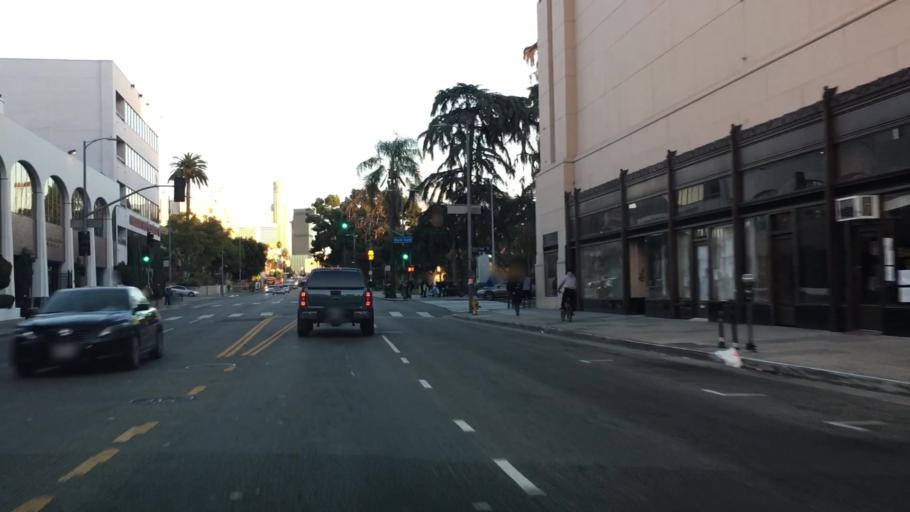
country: US
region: California
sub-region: Los Angeles County
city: Echo Park
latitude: 34.0614
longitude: -118.2790
